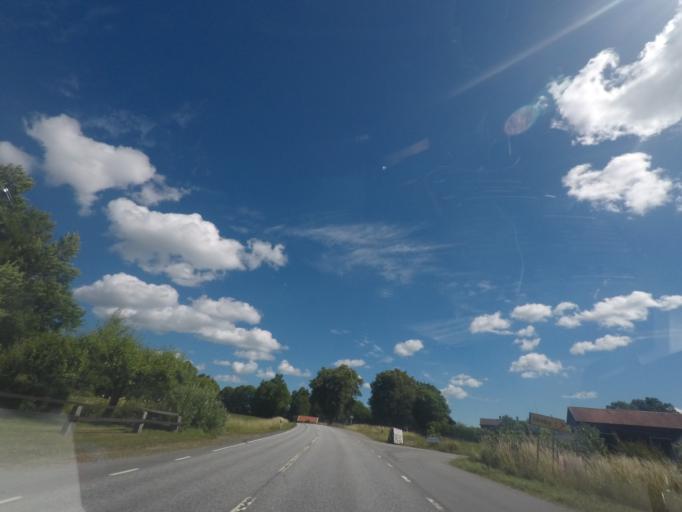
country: SE
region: Stockholm
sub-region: Norrtalje Kommun
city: Hallstavik
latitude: 59.9392
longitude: 18.7423
